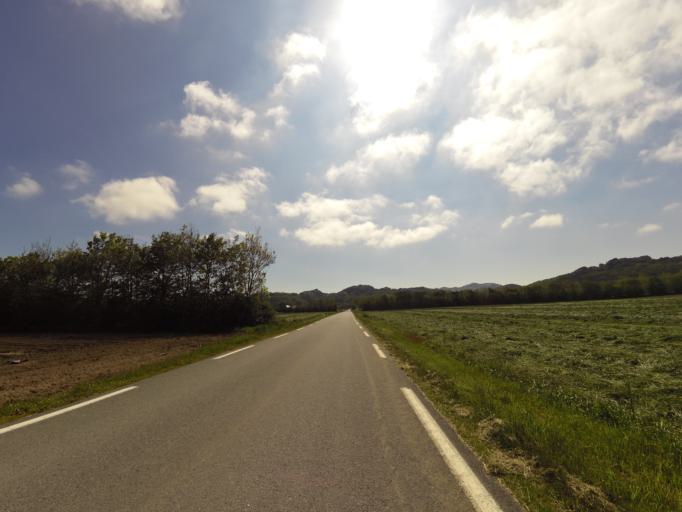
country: NO
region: Rogaland
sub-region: Ha
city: Vigrestad
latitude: 58.5196
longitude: 5.8121
